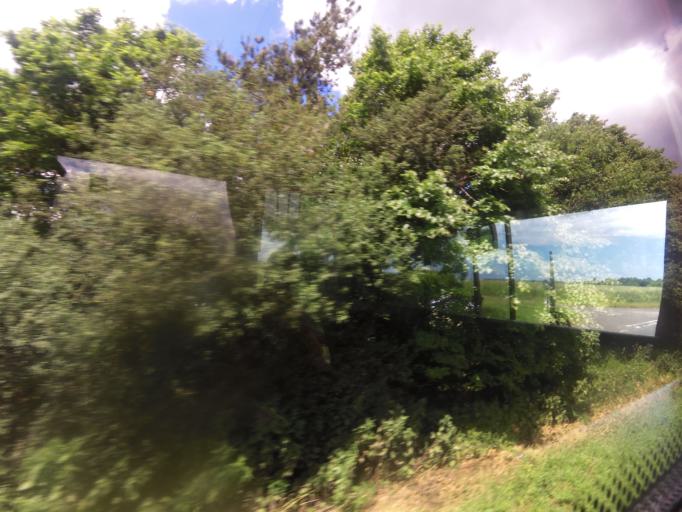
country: GB
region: England
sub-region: Norfolk
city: Cromer
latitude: 52.8725
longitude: 1.2869
